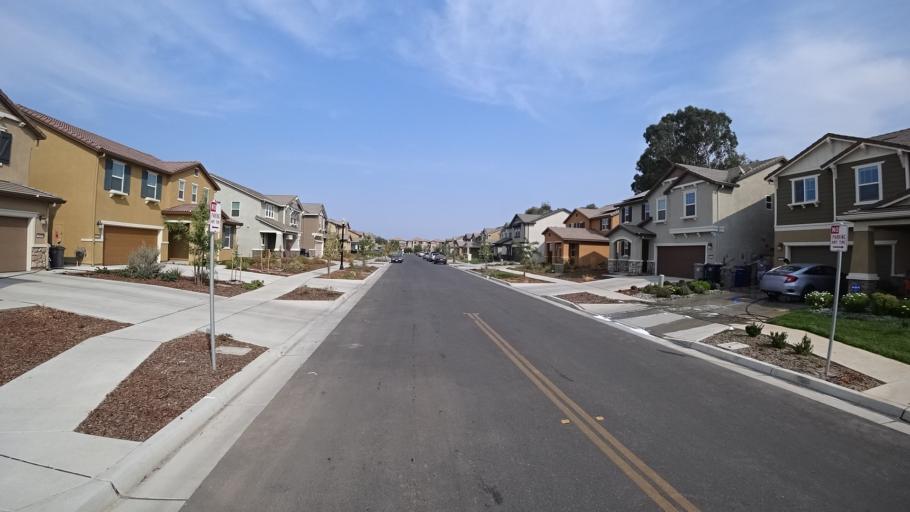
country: US
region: California
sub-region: Sacramento County
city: Laguna
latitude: 38.4507
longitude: -121.4120
